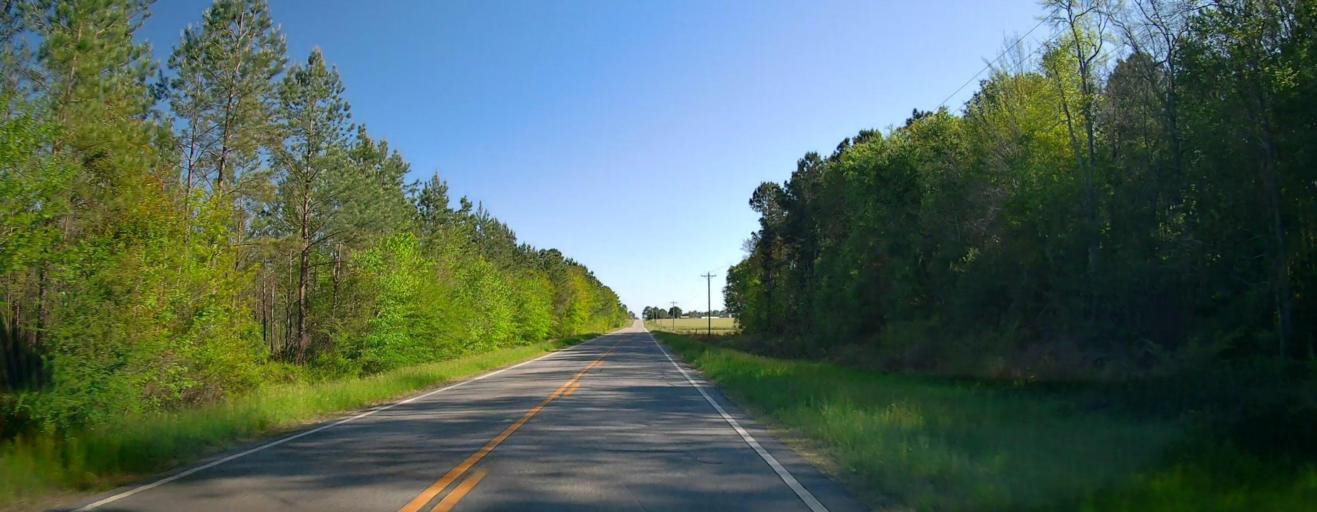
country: US
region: Georgia
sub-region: Wilcox County
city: Rochelle
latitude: 31.8674
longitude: -83.4888
